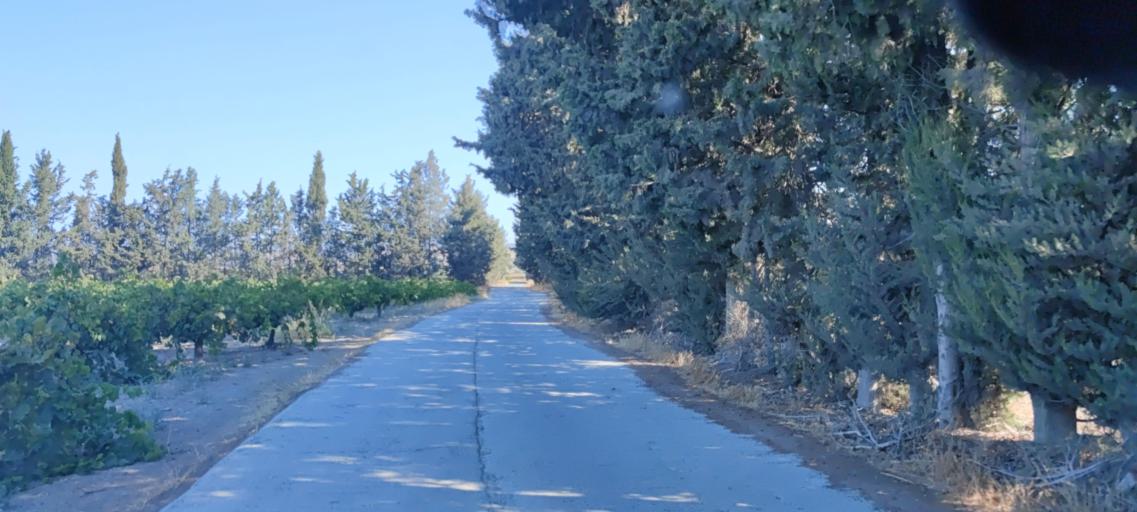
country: CY
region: Limassol
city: Sotira
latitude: 34.6690
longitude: 32.7973
